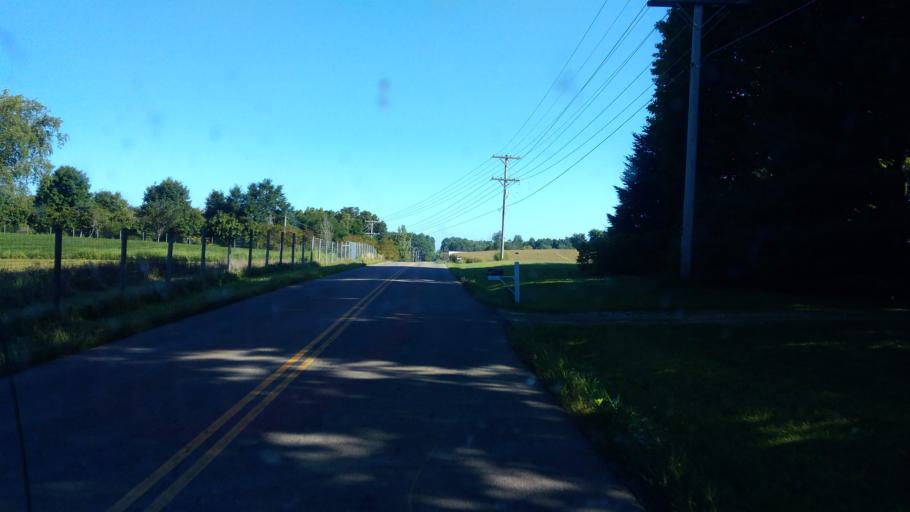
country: US
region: Ohio
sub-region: Knox County
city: Gambier
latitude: 40.4562
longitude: -82.3656
